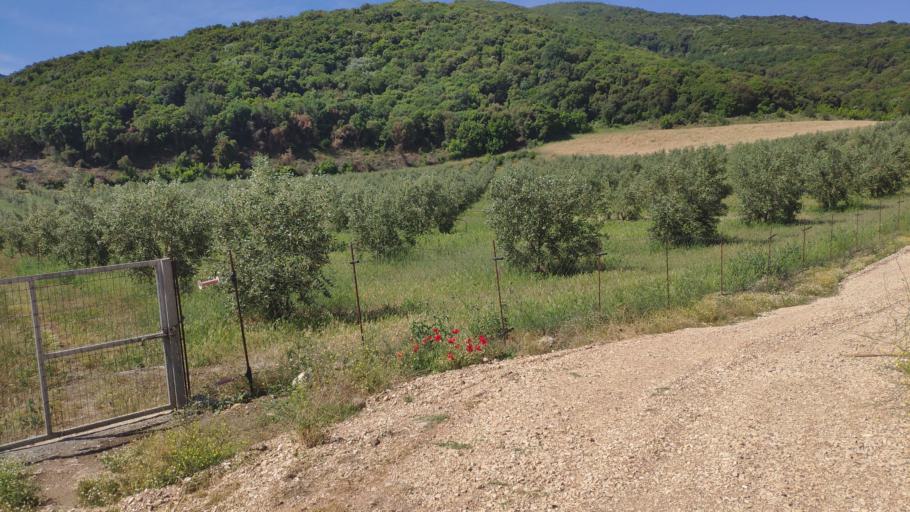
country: GR
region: West Greece
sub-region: Nomos Aitolias kai Akarnanias
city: Monastirakion
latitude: 38.8661
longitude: 21.0501
